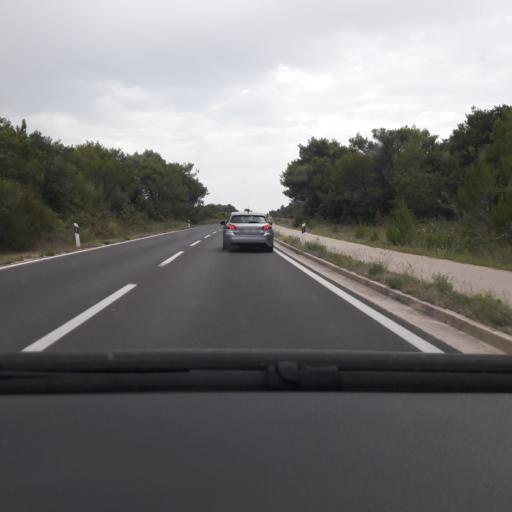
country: HR
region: Zadarska
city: Nin
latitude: 44.1817
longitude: 15.1869
